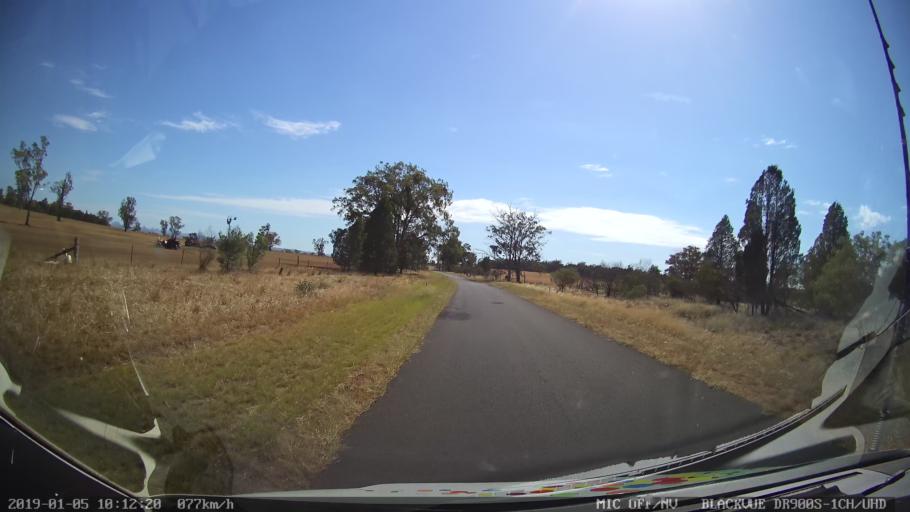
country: AU
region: New South Wales
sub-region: Gilgandra
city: Gilgandra
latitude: -31.6085
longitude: 148.9118
